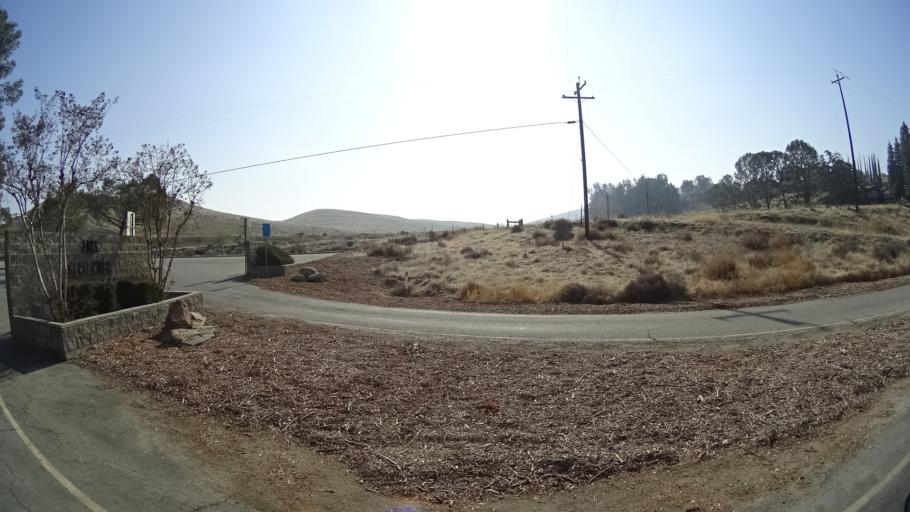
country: US
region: California
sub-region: Kern County
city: Oildale
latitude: 35.4330
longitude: -118.8606
